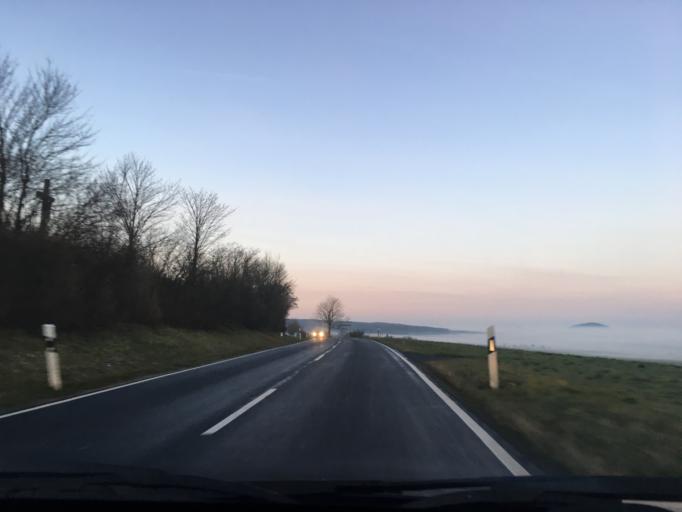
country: DE
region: Hesse
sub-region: Regierungsbezirk Kassel
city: Hofbieber
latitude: 50.5887
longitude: 9.8232
